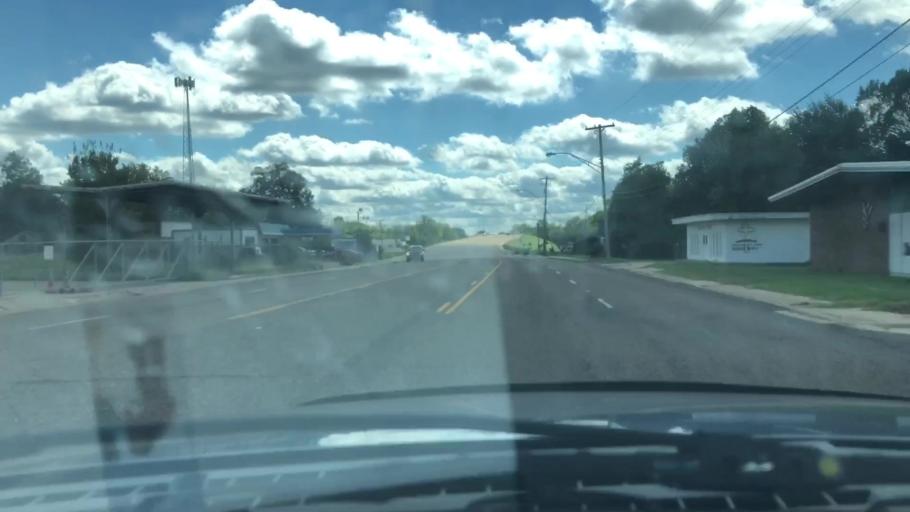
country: US
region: Texas
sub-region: Bowie County
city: Texarkana
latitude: 33.4185
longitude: -94.0612
